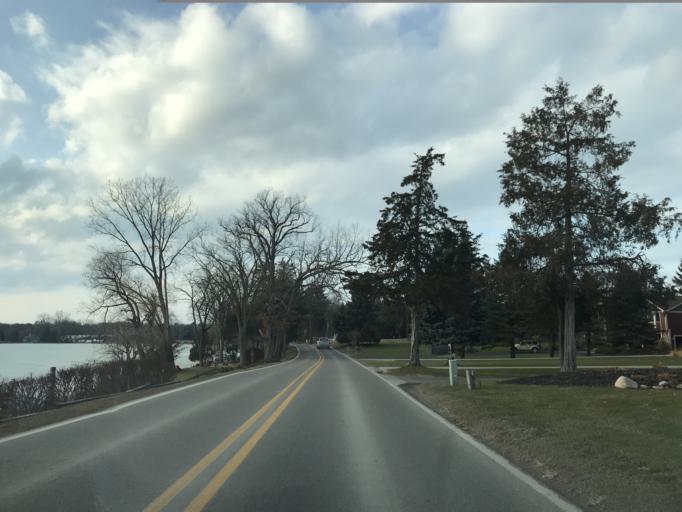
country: US
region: Michigan
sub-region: Livingston County
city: Whitmore Lake
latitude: 42.4691
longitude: -83.7182
